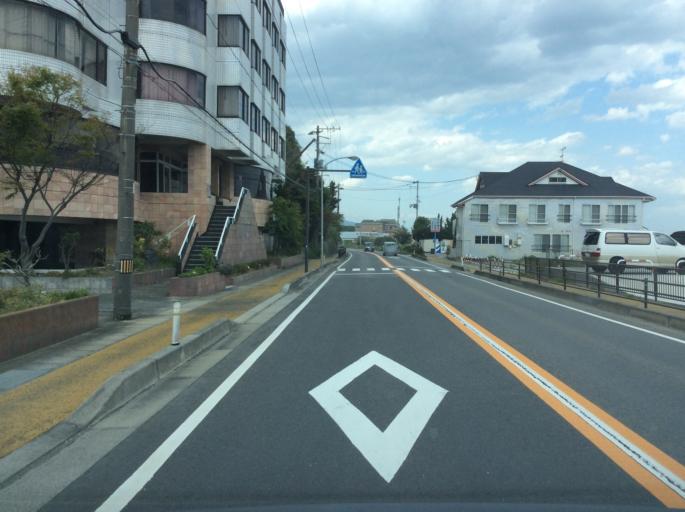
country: JP
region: Ibaraki
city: Kitaibaraki
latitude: 36.8700
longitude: 140.7887
